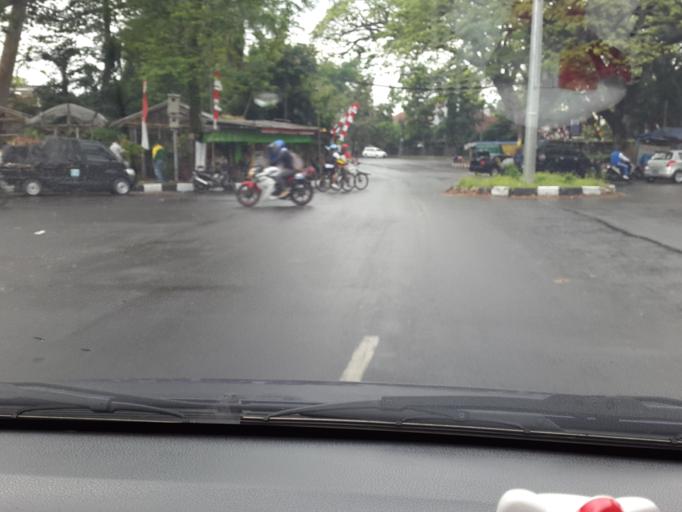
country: ID
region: West Java
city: Bandung
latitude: -6.9059
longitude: 107.6242
